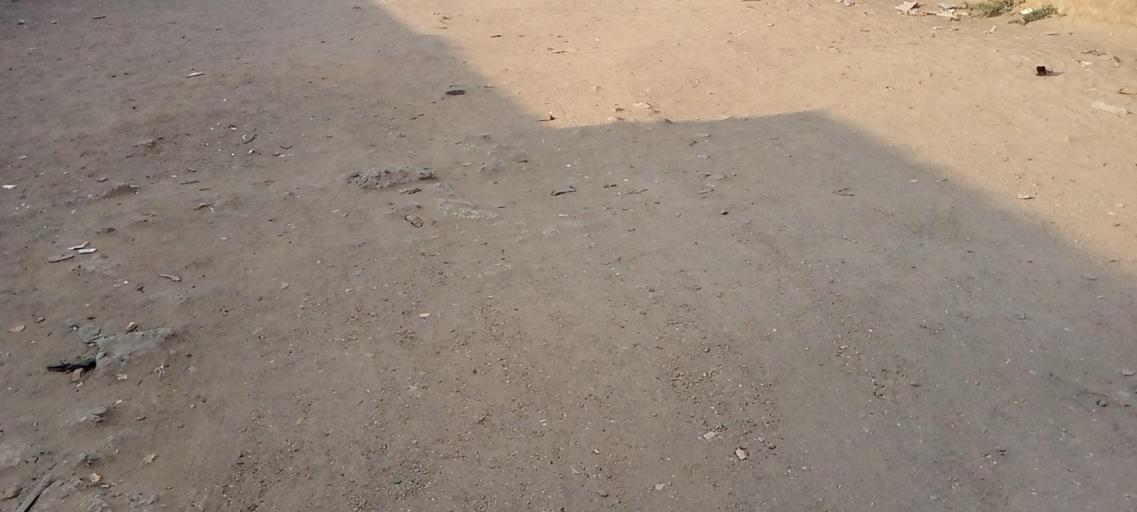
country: ZM
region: Lusaka
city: Lusaka
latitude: -15.4032
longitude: 28.3547
